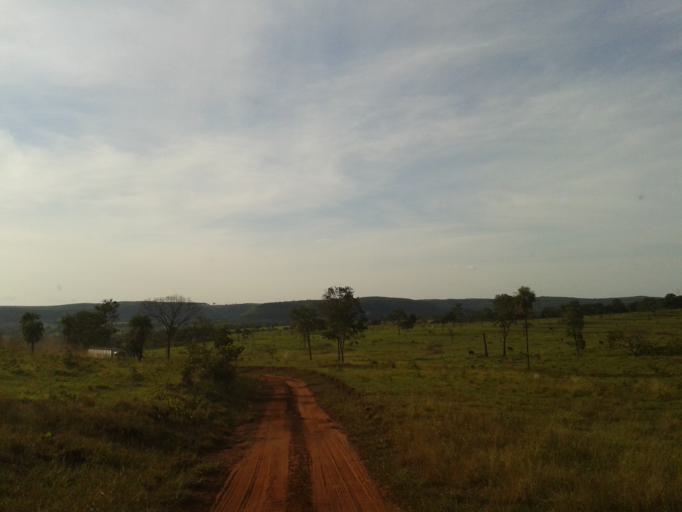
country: BR
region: Minas Gerais
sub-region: Campina Verde
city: Campina Verde
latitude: -19.4946
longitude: -49.6062
